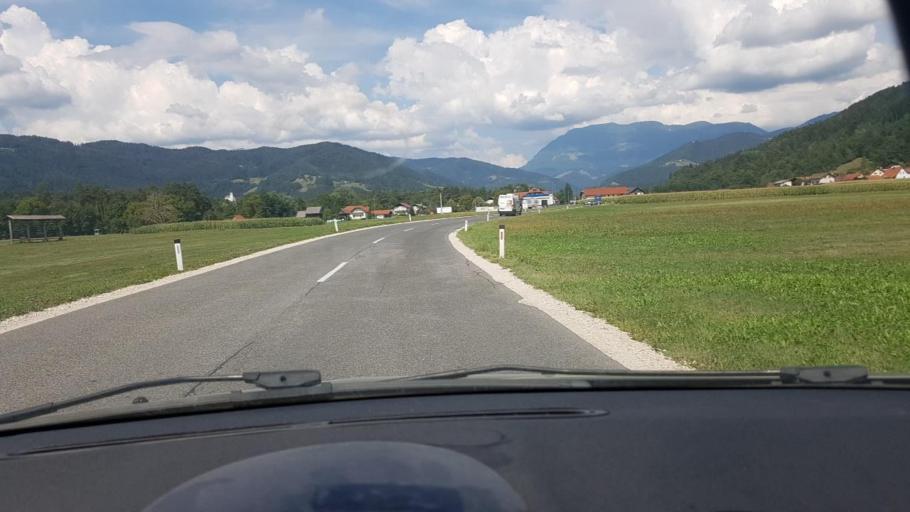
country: SI
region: Recica ob Savinji
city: Recica ob Savinji
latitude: 46.3200
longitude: 14.8742
